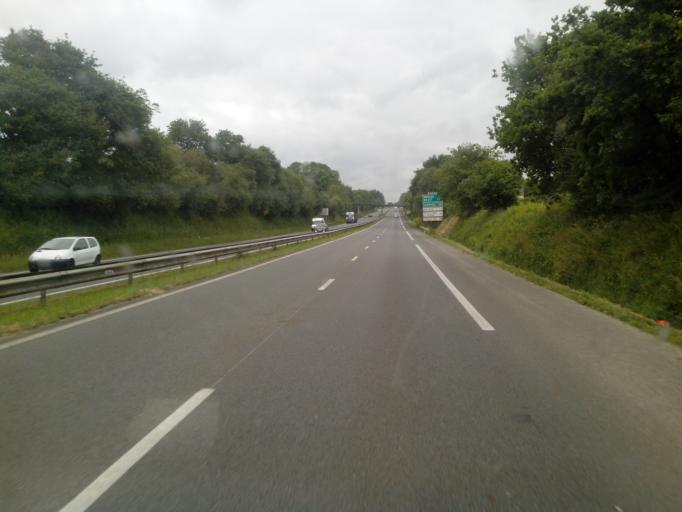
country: FR
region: Brittany
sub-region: Departement des Cotes-d'Armor
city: Graces
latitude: 48.5558
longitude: -3.1761
